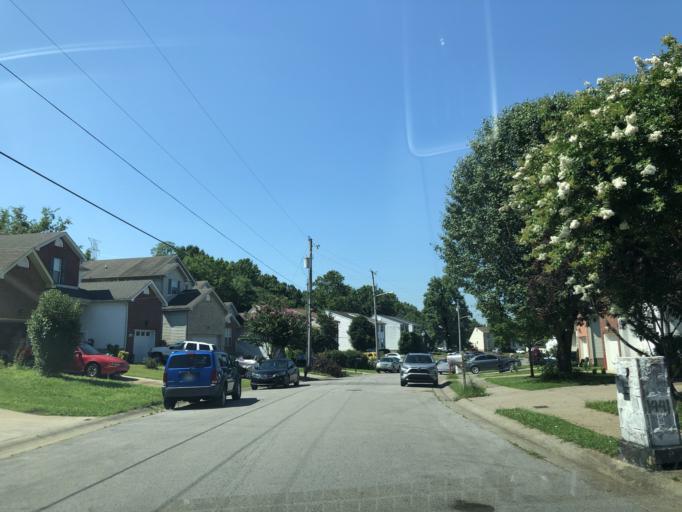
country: US
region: Tennessee
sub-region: Williamson County
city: Nolensville
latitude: 36.0404
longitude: -86.6705
